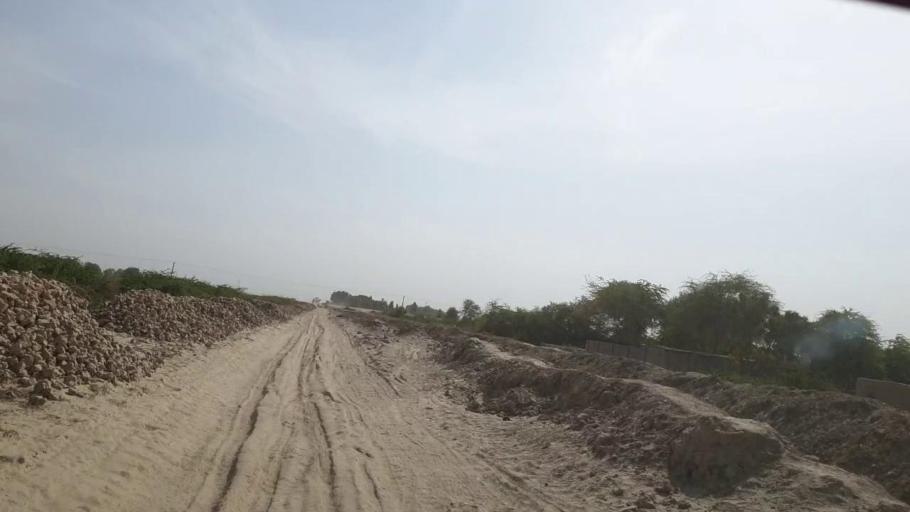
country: PK
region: Sindh
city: Nabisar
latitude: 25.0604
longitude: 69.5774
